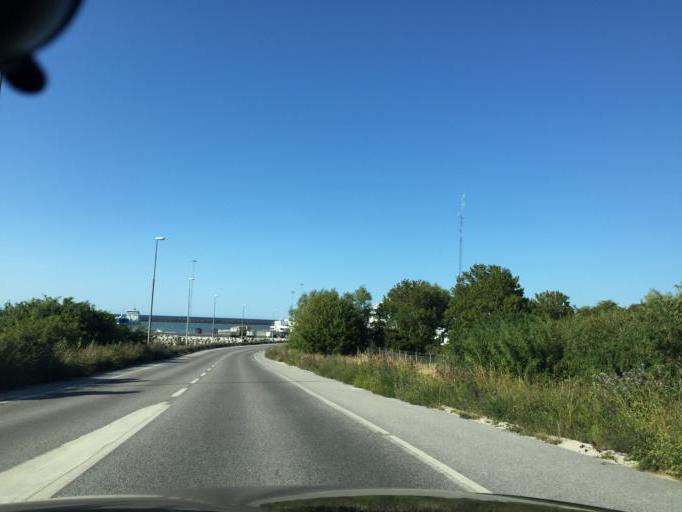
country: SE
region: Gotland
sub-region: Gotland
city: Visby
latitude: 57.6274
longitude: 18.2747
